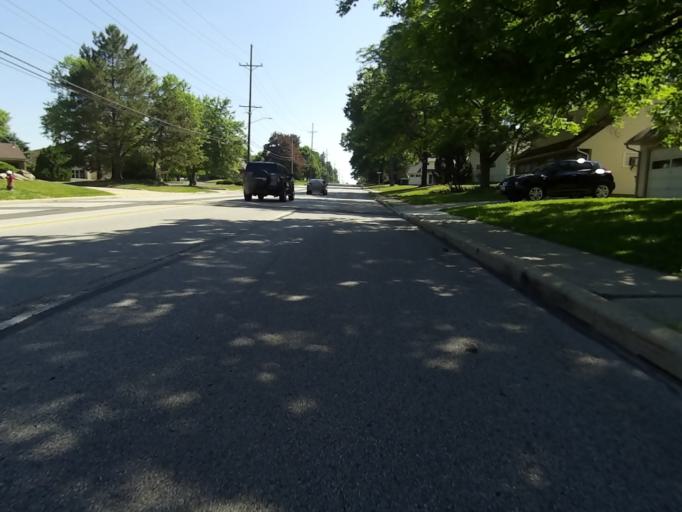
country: US
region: Ohio
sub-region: Summit County
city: Cuyahoga Falls
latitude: 41.1547
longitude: -81.4987
